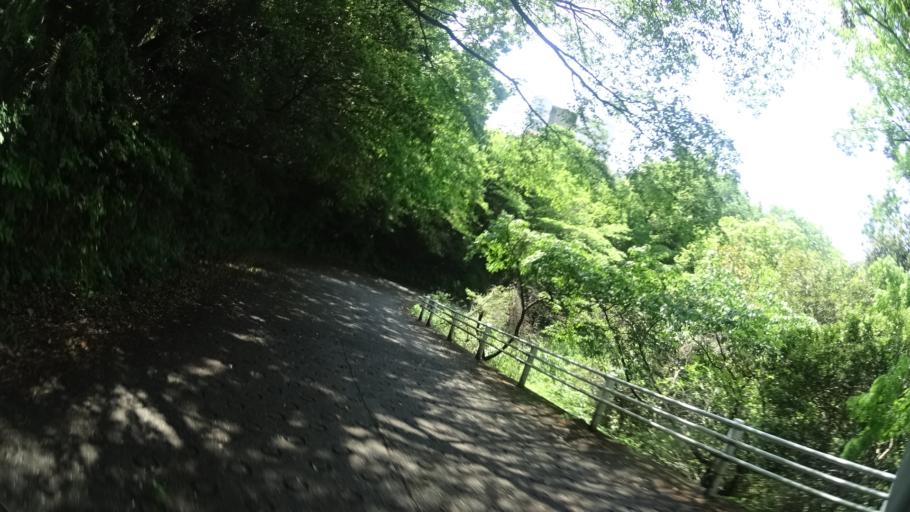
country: JP
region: Tokushima
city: Tokushima-shi
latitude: 34.0681
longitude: 134.5313
